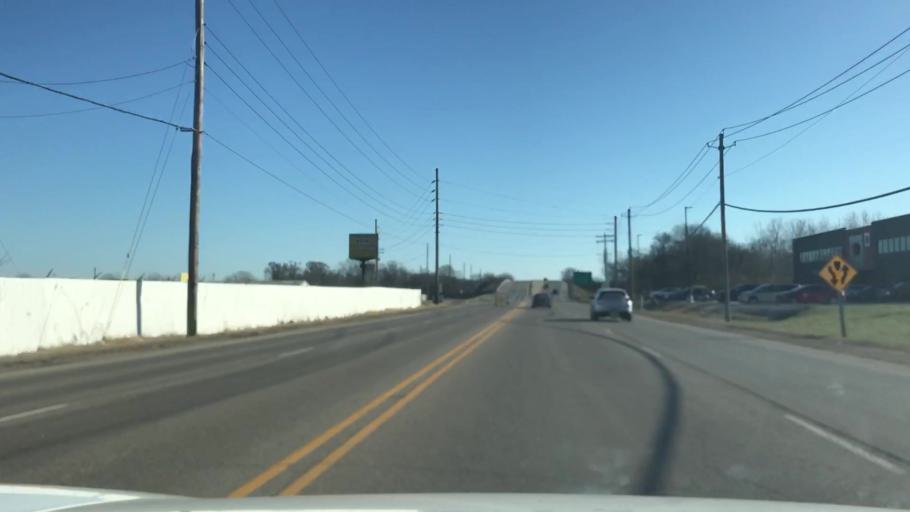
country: US
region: Illinois
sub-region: Saint Clair County
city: Alorton
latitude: 38.5966
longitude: -90.1240
